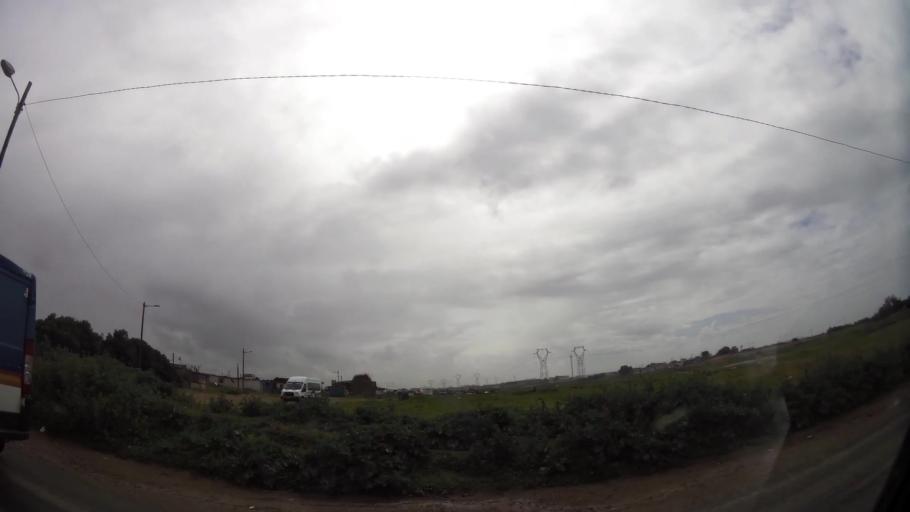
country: MA
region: Grand Casablanca
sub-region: Mediouna
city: Tit Mellil
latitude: 33.6402
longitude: -7.4756
